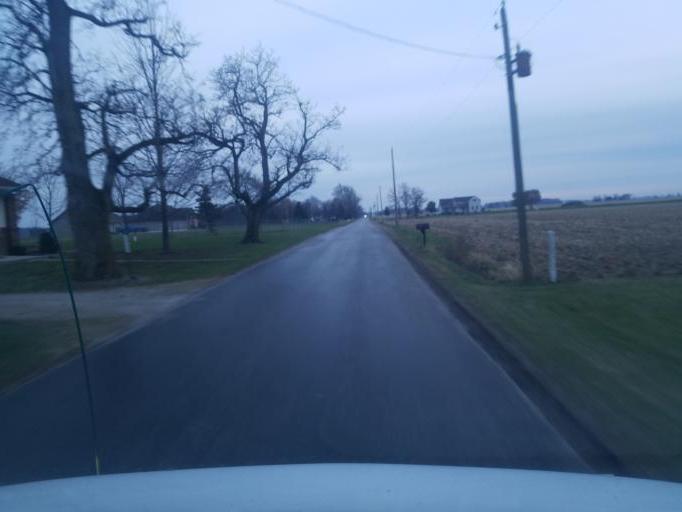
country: US
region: Indiana
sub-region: Adams County
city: Decatur
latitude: 40.7852
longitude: -85.0148
